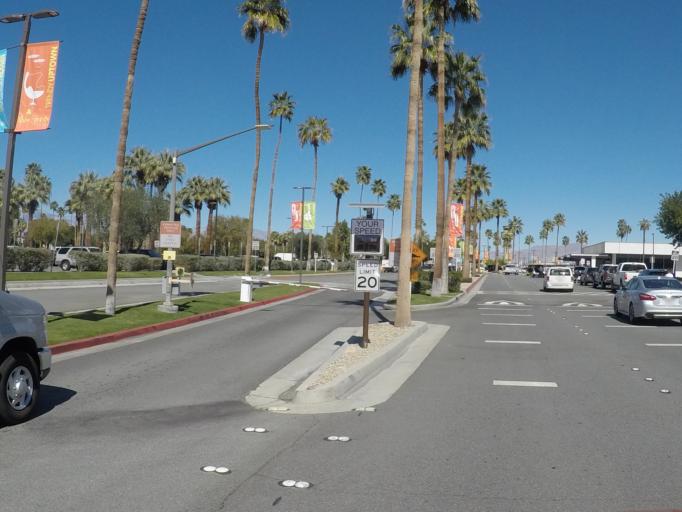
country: US
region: California
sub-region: Riverside County
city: Palm Springs
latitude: 33.8214
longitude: -116.5088
